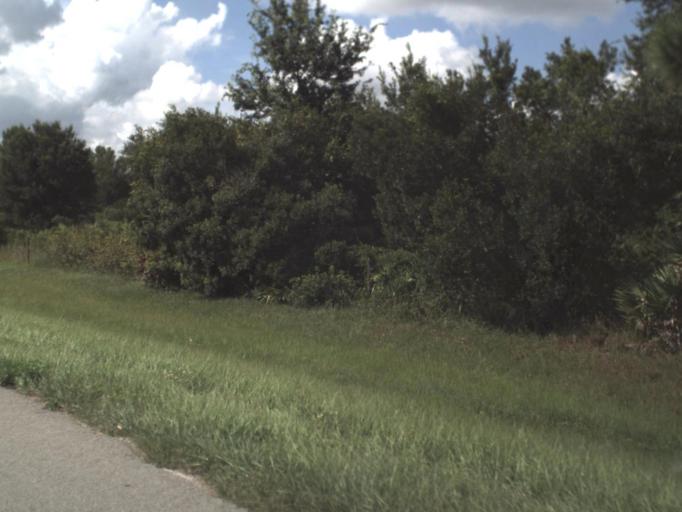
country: US
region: Florida
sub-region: Hillsborough County
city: Wimauma
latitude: 27.4718
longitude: -82.2033
